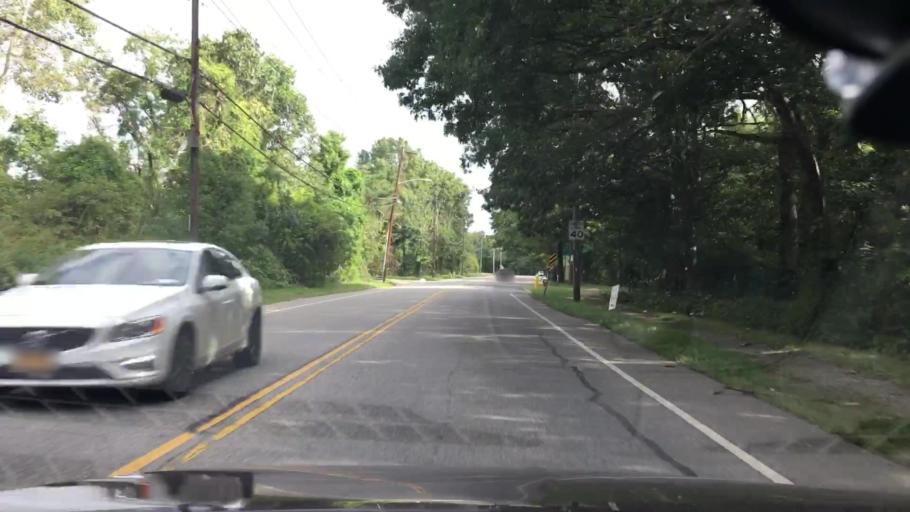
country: US
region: New York
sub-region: Nassau County
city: Old Bethpage
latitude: 40.7772
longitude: -73.4464
